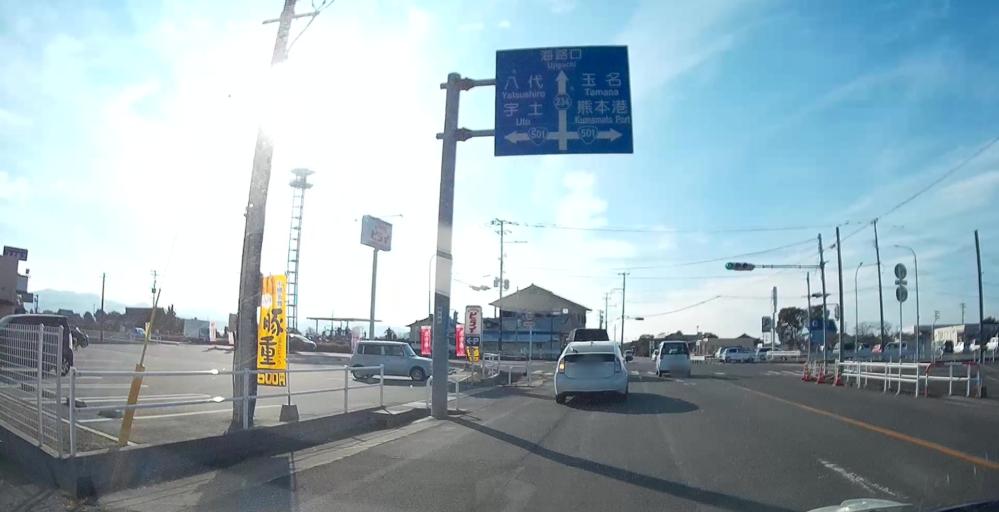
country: JP
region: Kumamoto
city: Uto
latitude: 32.7314
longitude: 130.6398
